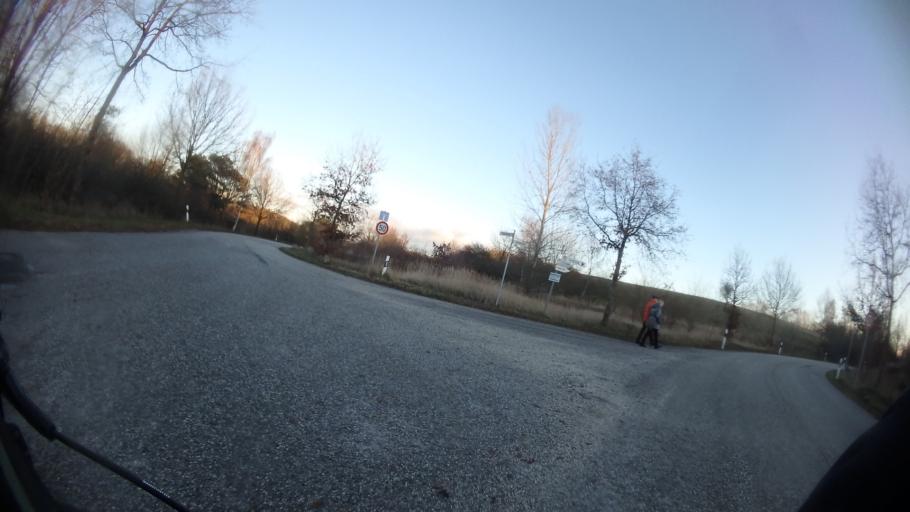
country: DE
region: Mecklenburg-Vorpommern
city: Selmsdorf
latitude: 53.9258
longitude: 10.8300
